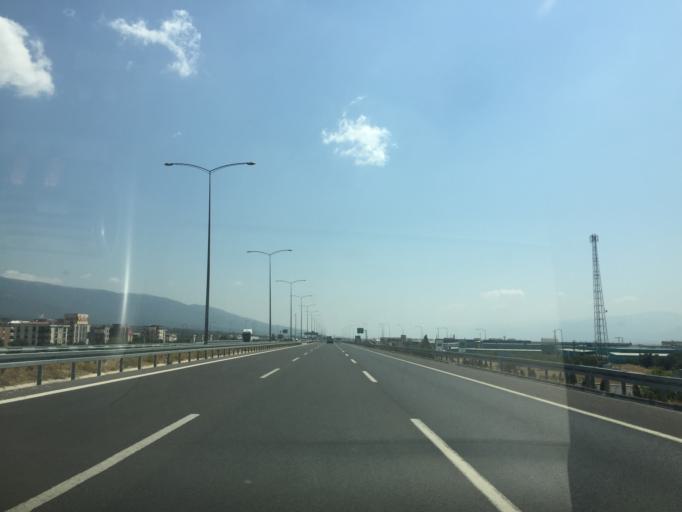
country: TR
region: Izmir
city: Kemalpasa
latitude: 38.4704
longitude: 27.3523
